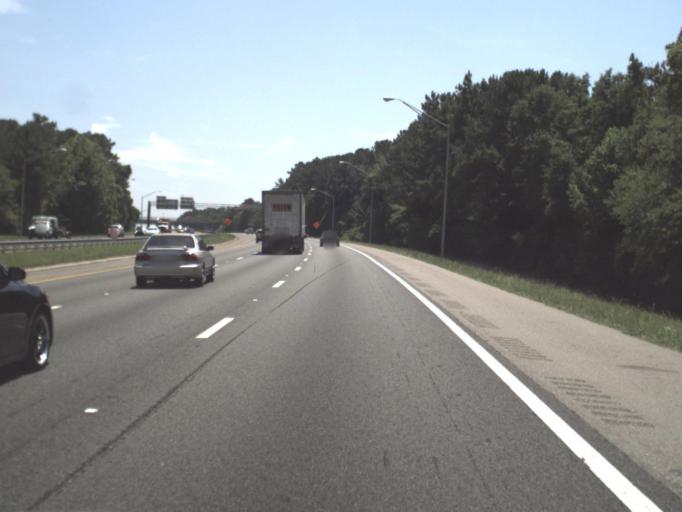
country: US
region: Florida
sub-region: Clay County
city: Bellair-Meadowbrook Terrace
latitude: 30.2832
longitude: -81.7719
